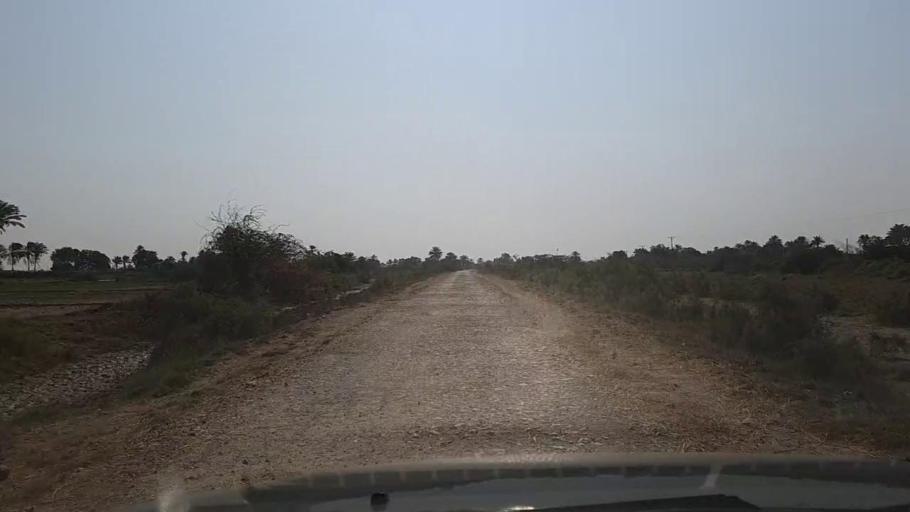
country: PK
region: Sindh
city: Mirpur Sakro
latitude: 24.3997
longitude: 67.6668
